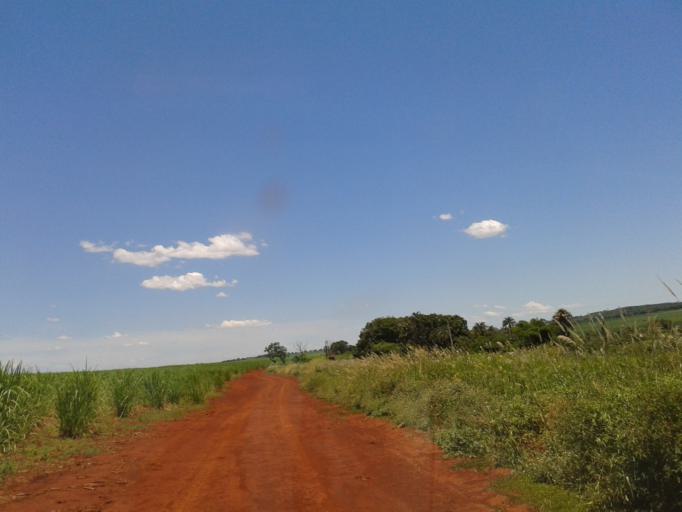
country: BR
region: Minas Gerais
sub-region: Centralina
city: Centralina
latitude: -18.6699
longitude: -49.2412
